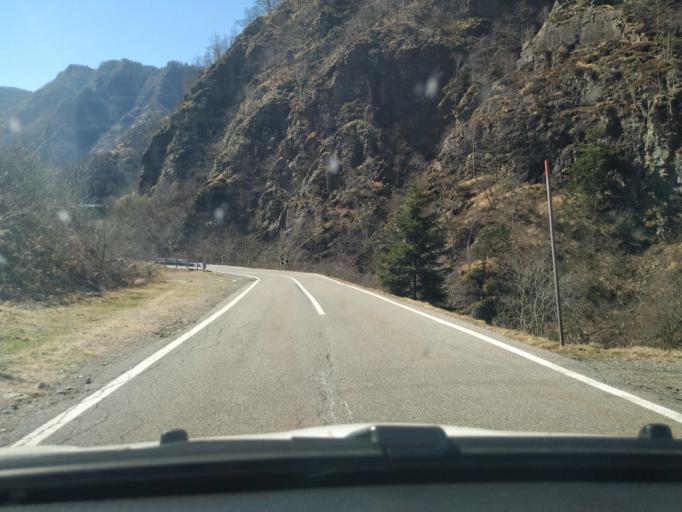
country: IT
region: Piedmont
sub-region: Provincia di Vercelli
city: Cervatto
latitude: 45.8882
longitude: 8.1788
